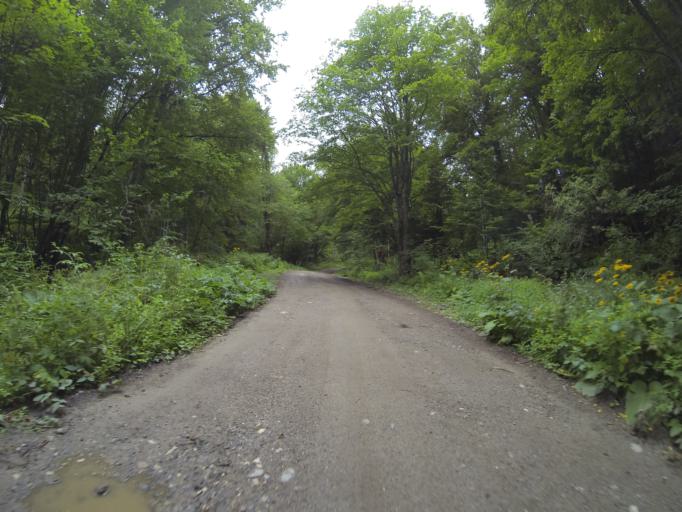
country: RO
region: Brasov
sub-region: Comuna Sinca Veche
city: Sinca Veche
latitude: 45.6961
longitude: 25.1660
